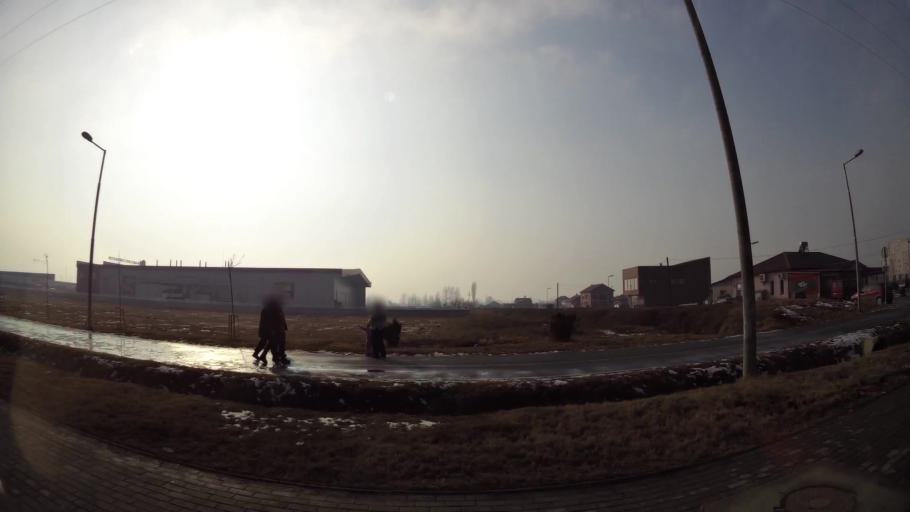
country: MK
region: Ilinden
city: Marino
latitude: 41.9862
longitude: 21.5893
